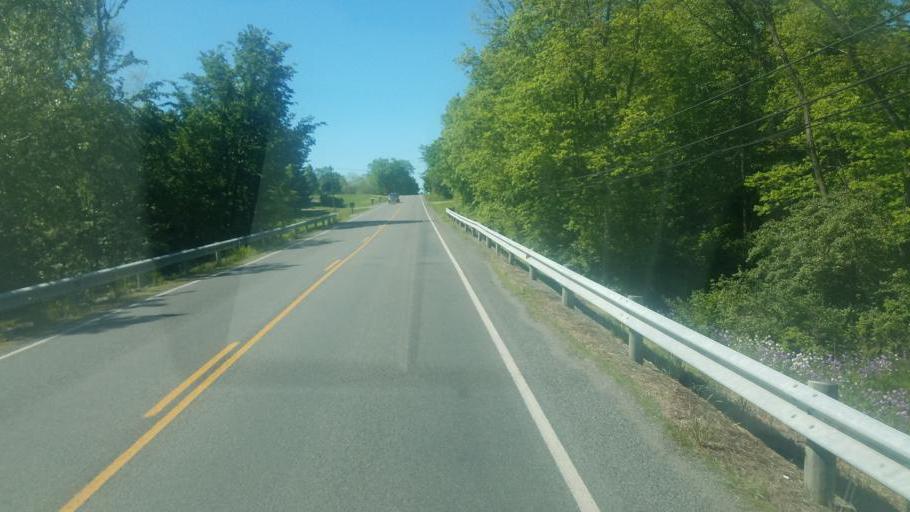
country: US
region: Ohio
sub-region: Logan County
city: Bellefontaine
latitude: 40.3737
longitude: -83.7787
